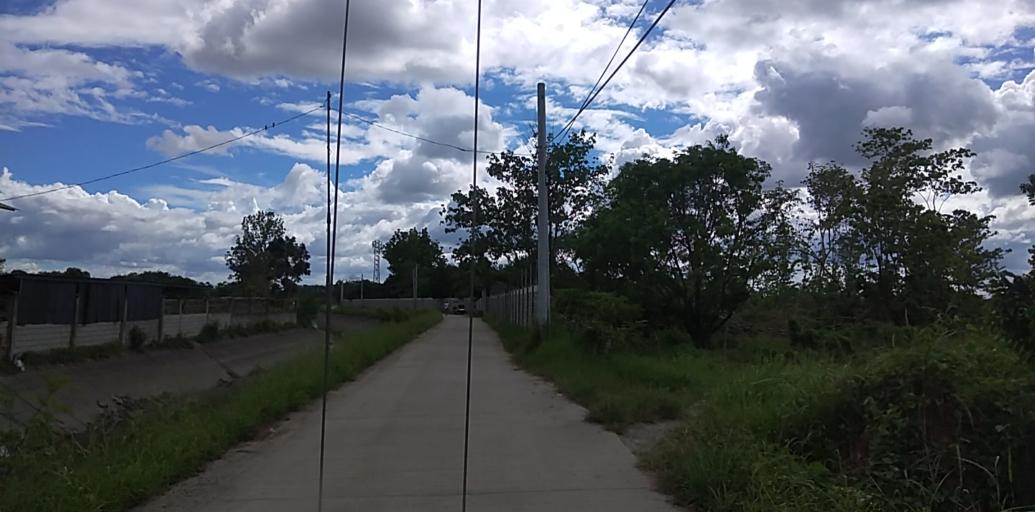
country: PH
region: Central Luzon
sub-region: Province of Pampanga
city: Arayat
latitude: 15.1380
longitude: 120.7783
